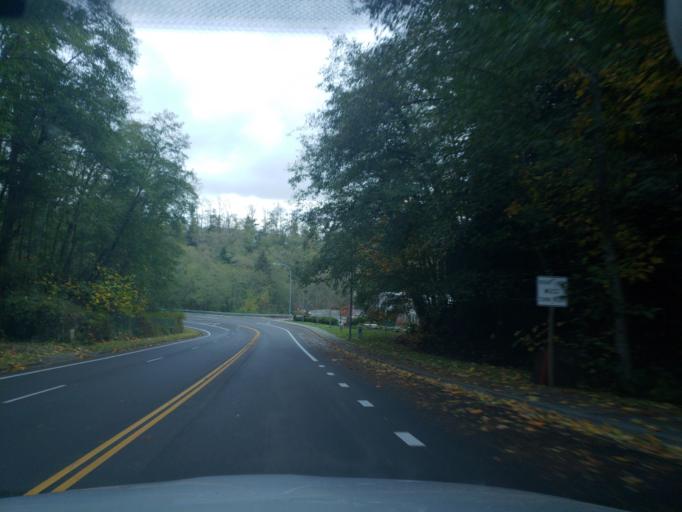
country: US
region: Washington
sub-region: Snohomish County
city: Mukilteo
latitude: 47.9396
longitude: -122.2728
